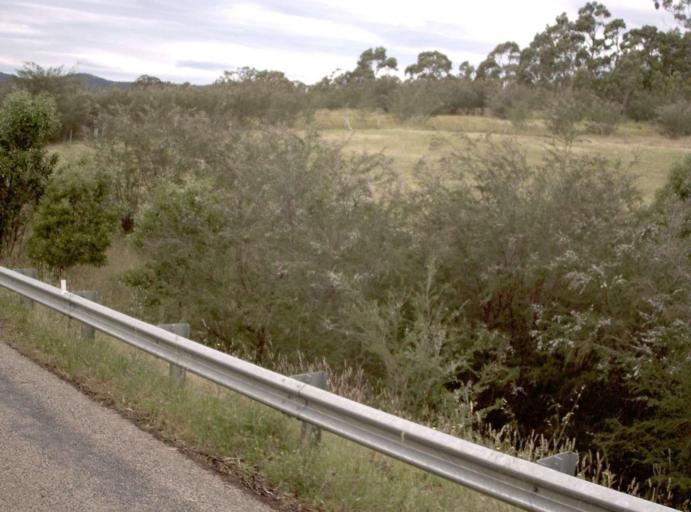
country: AU
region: Victoria
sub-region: East Gippsland
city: Bairnsdale
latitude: -37.4727
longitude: 147.2303
